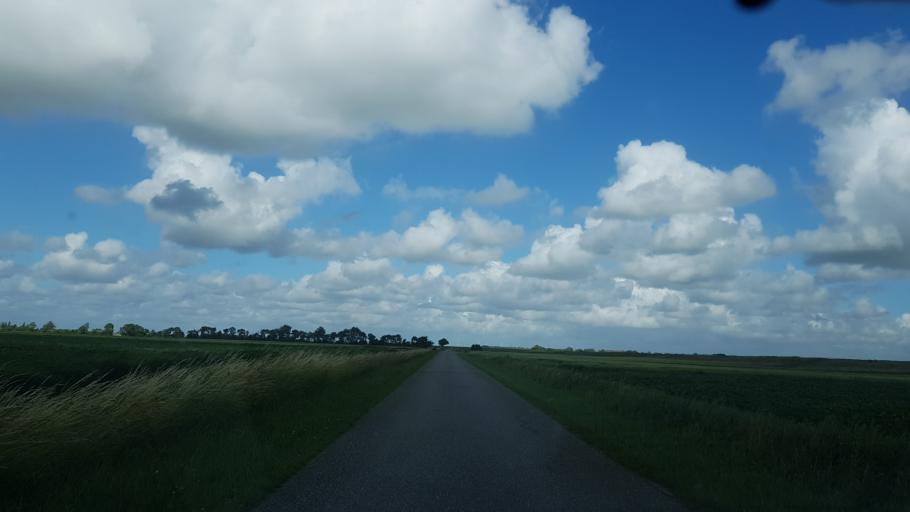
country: NL
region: Groningen
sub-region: Gemeente Bedum
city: Bedum
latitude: 53.4232
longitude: 6.6340
